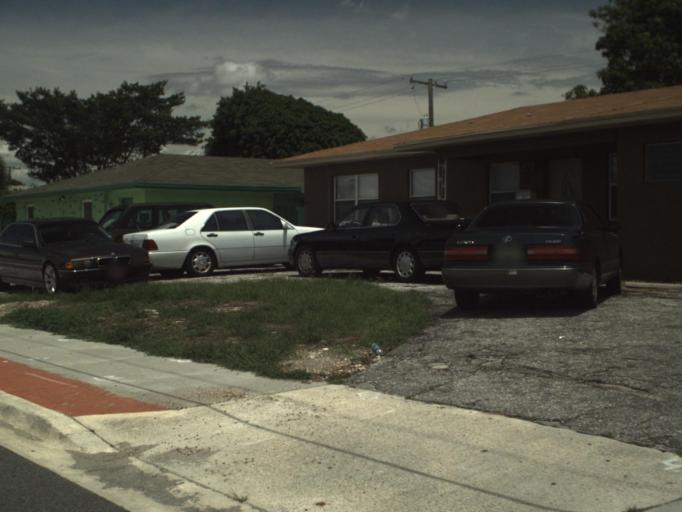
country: US
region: Florida
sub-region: Palm Beach County
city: Riviera Beach
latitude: 26.7836
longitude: -80.0605
